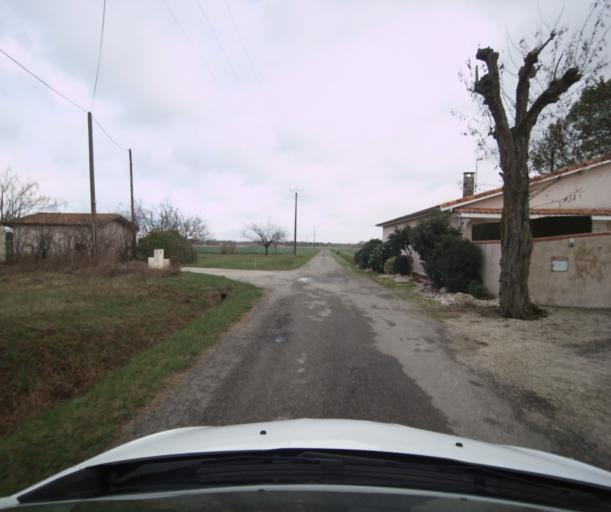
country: FR
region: Midi-Pyrenees
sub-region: Departement du Tarn-et-Garonne
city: Saint-Porquier
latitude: 44.0635
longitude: 1.1645
